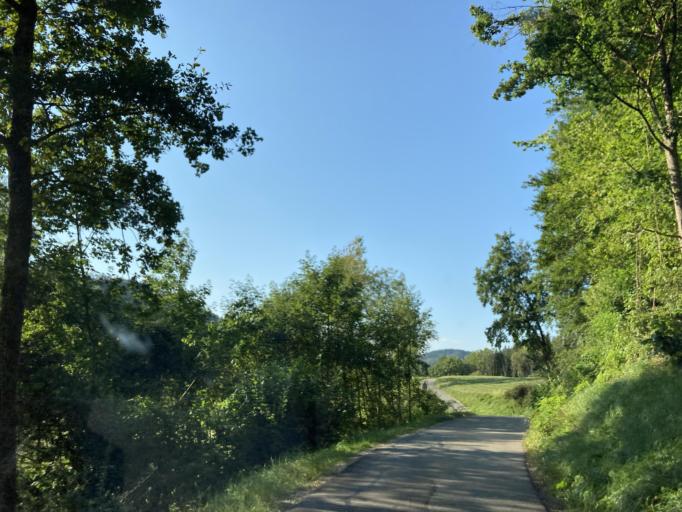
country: DE
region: Baden-Wuerttemberg
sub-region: Freiburg Region
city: Blumberg
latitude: 47.8262
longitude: 8.5095
